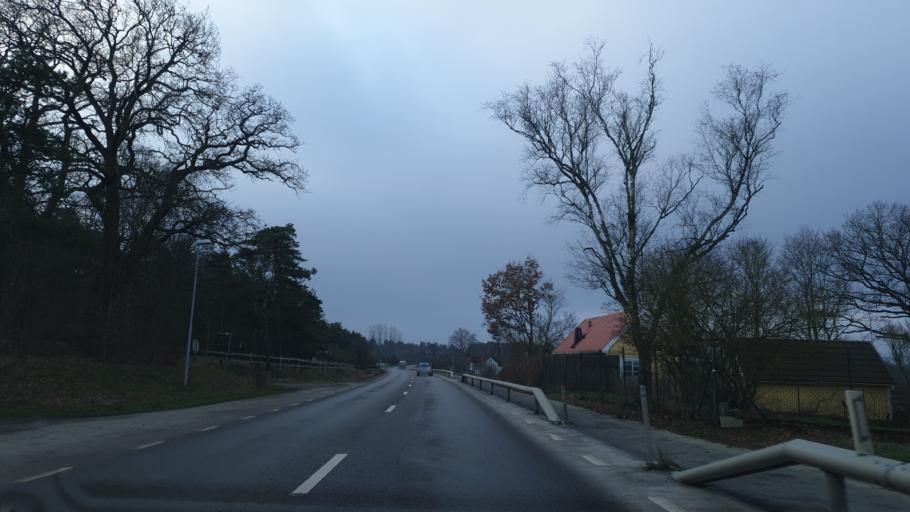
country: SE
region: Blekinge
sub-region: Solvesborgs Kommun
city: Soelvesborg
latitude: 56.1055
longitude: 14.6709
